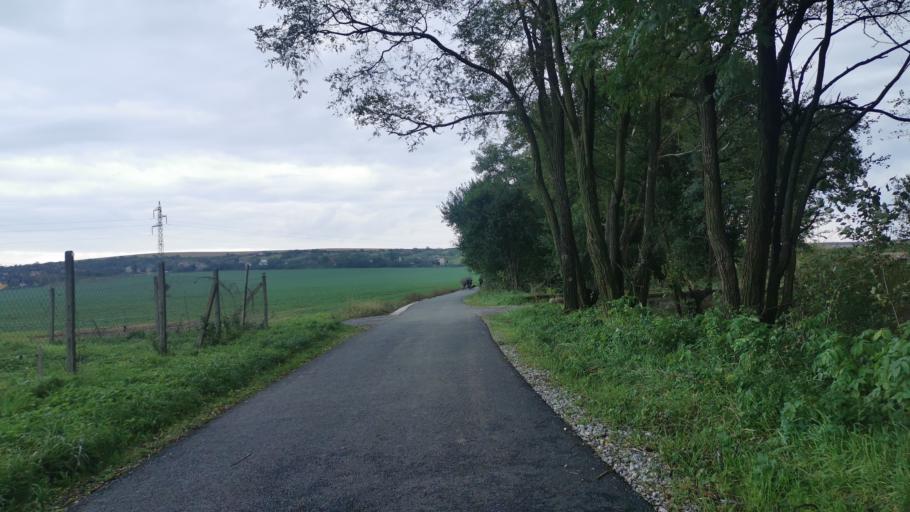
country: SK
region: Trnavsky
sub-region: Okres Skalica
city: Holic
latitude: 48.8051
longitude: 17.2019
